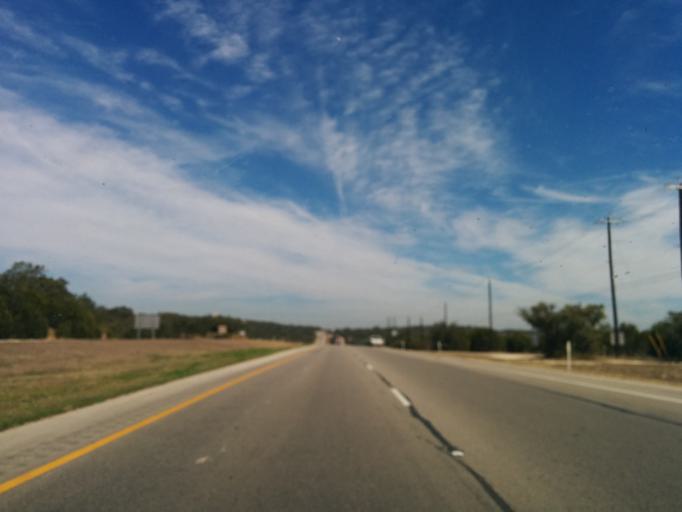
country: US
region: Texas
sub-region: Comal County
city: Bulverde
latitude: 29.7479
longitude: -98.4322
